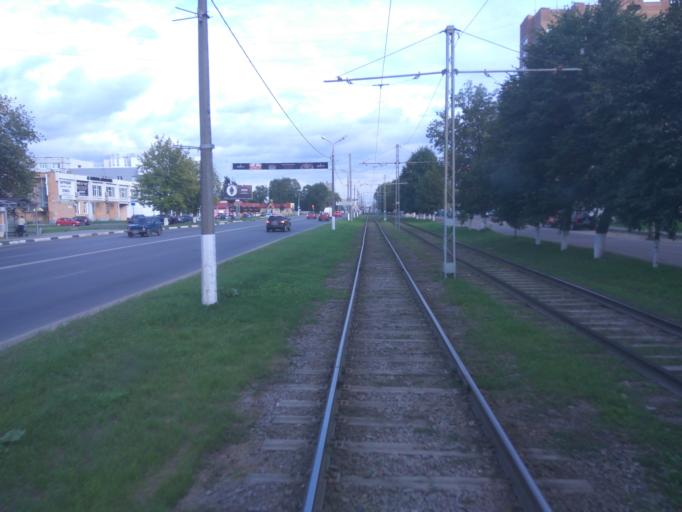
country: RU
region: Moskovskaya
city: Kolomna
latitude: 55.0869
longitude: 38.7930
